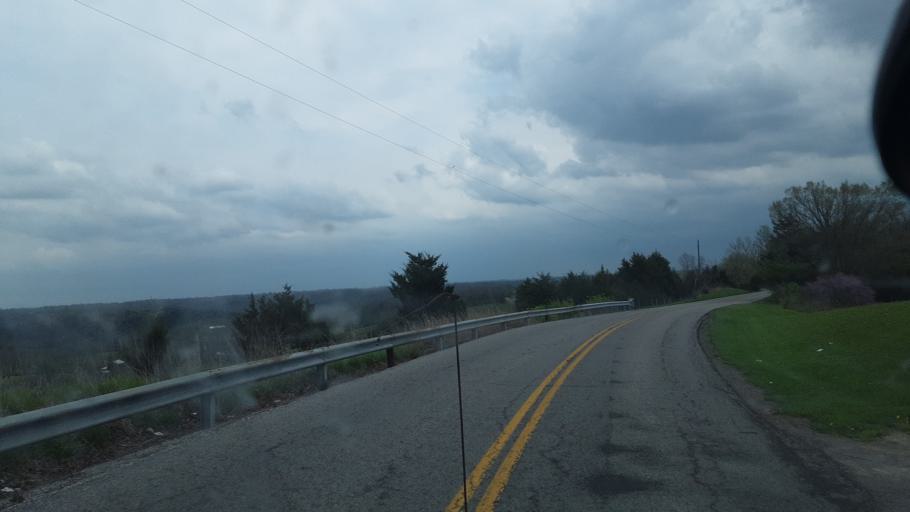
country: US
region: Kentucky
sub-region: Grant County
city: Dry Ridge
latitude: 38.6491
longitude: -84.7381
